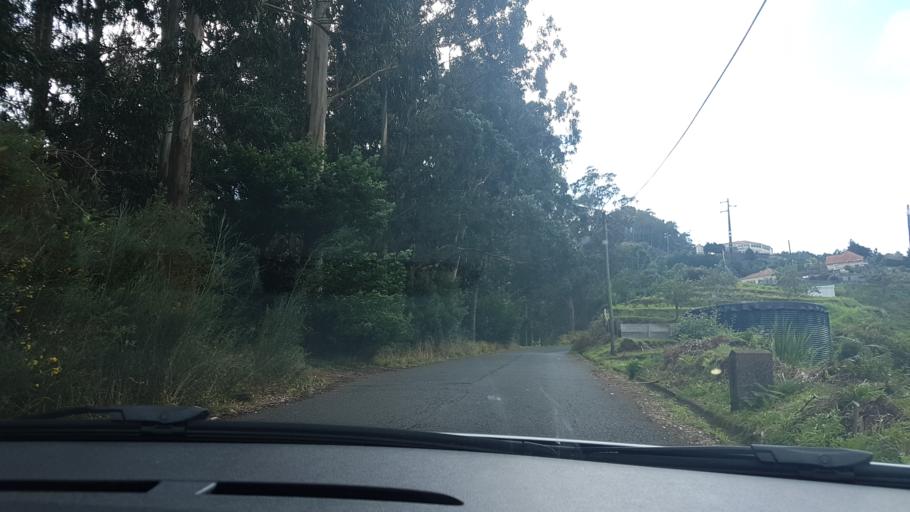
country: PT
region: Madeira
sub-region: Santa Cruz
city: Santa Cruz
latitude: 32.7321
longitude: -16.8228
